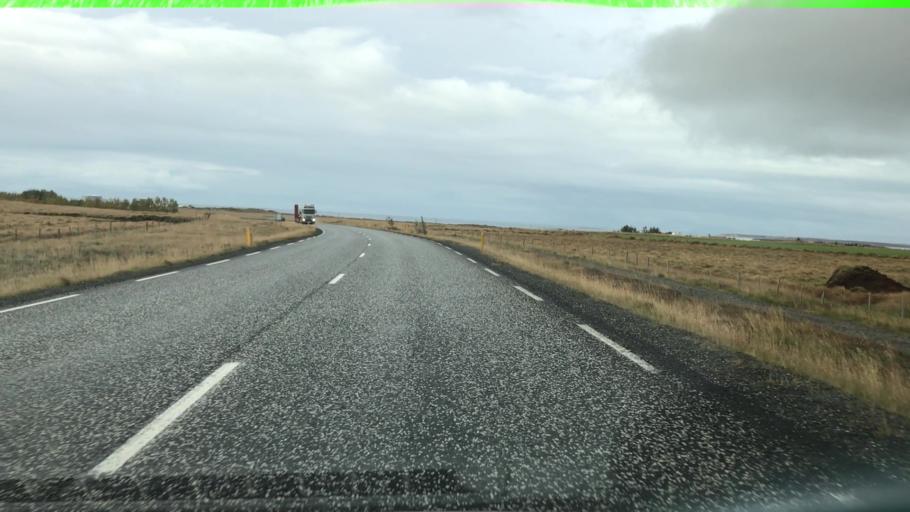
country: IS
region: West
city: Akranes
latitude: 64.3232
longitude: -22.0143
